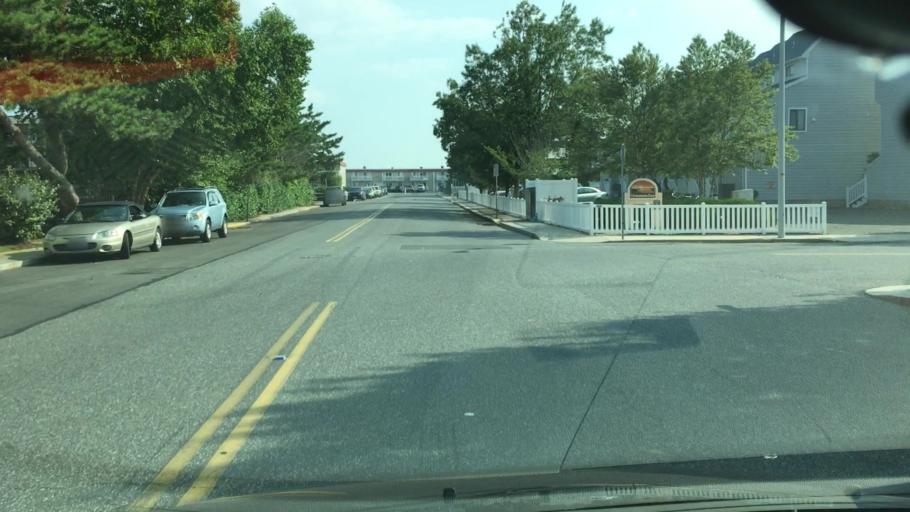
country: US
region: Maryland
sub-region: Worcester County
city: Ocean City
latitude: 38.4090
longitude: -75.0670
